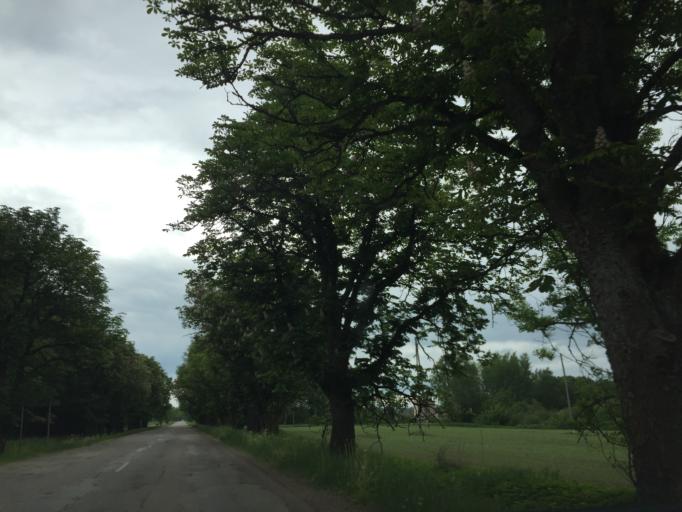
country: LV
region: Preilu Rajons
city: Preili
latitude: 56.0668
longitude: 26.7575
